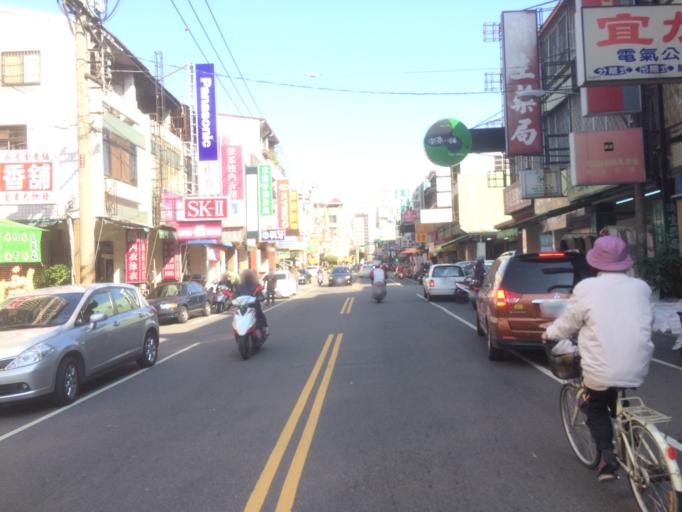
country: TW
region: Taiwan
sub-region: Taichung City
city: Taichung
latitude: 24.1781
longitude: 120.6906
